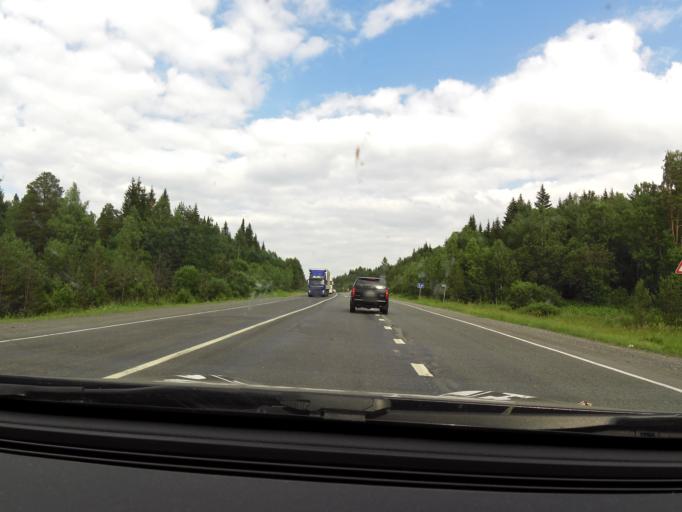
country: RU
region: Sverdlovsk
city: Druzhinino
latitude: 56.7975
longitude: 59.4537
